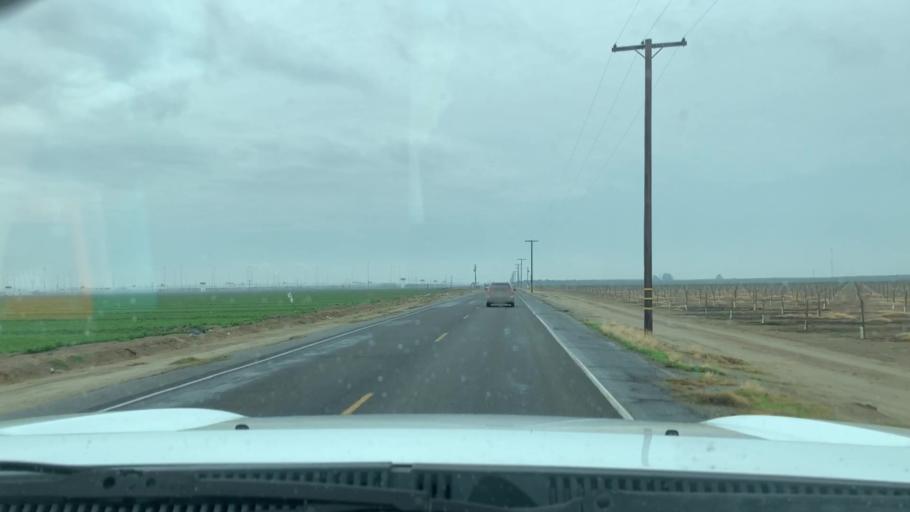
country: US
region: California
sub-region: Kern County
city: Delano
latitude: 35.7612
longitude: -119.3381
